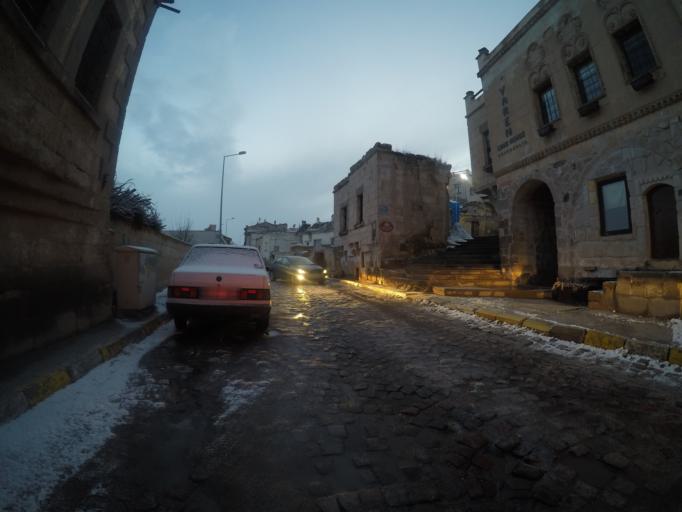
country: TR
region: Nevsehir
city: Goereme
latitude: 38.6292
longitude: 34.8057
